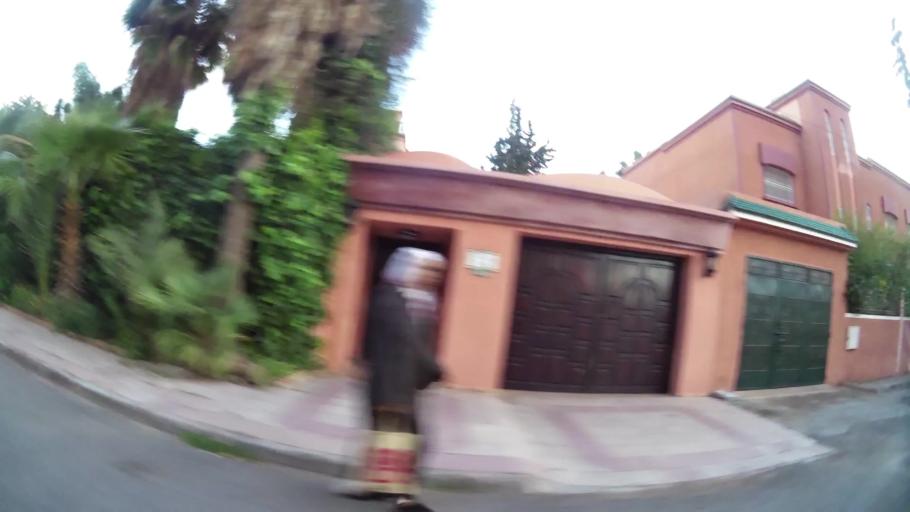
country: MA
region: Marrakech-Tensift-Al Haouz
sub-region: Marrakech
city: Marrakesh
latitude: 31.6434
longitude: -8.0216
